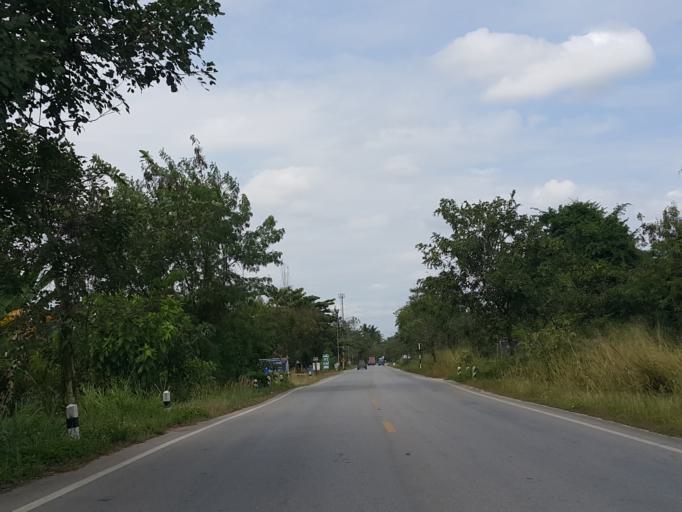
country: TH
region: Lampang
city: Lampang
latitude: 18.3329
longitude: 99.4613
